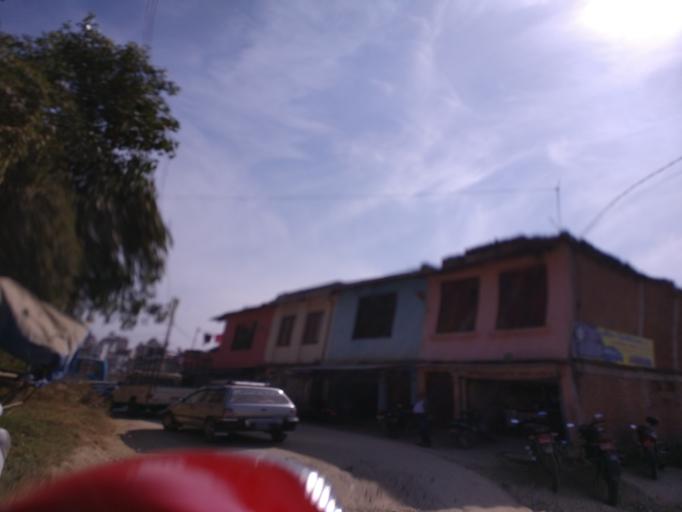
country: NP
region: Central Region
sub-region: Bagmati Zone
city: Patan
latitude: 27.6657
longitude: 85.3106
